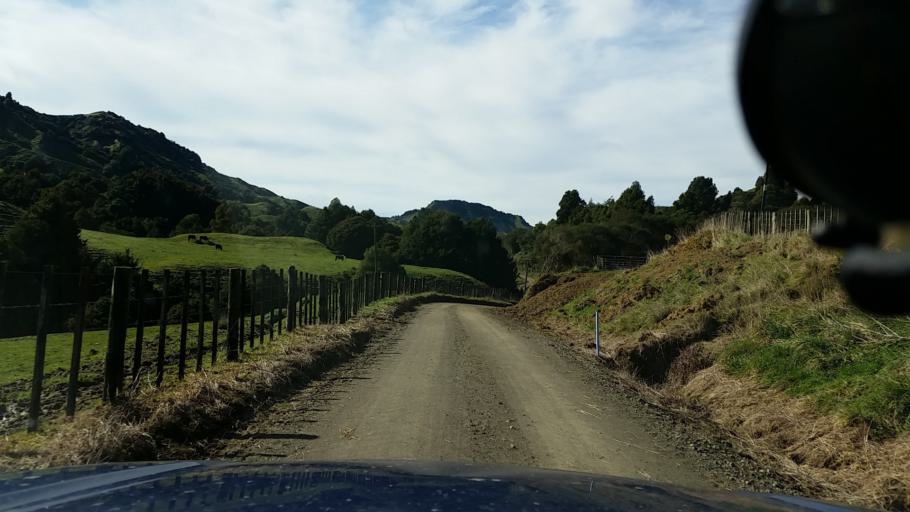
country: NZ
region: Taranaki
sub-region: New Plymouth District
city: Waitara
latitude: -39.0511
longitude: 174.7588
